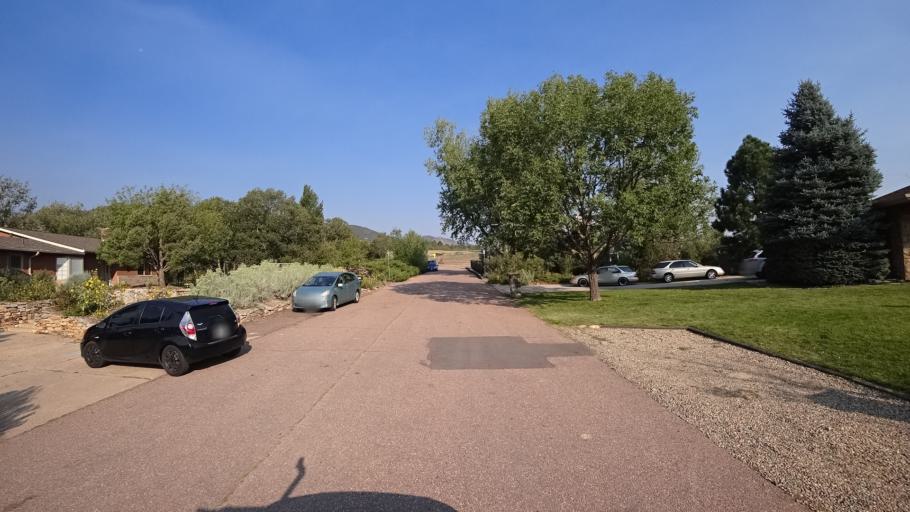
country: US
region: Colorado
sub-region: El Paso County
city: Colorado Springs
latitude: 38.8001
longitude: -104.8557
